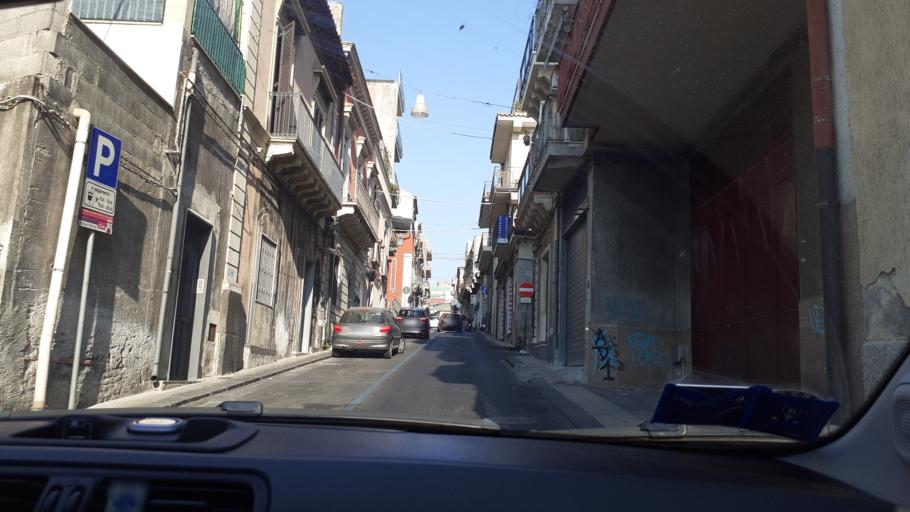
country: IT
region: Sicily
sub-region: Catania
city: Misterbianco
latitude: 37.5178
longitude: 15.0109
